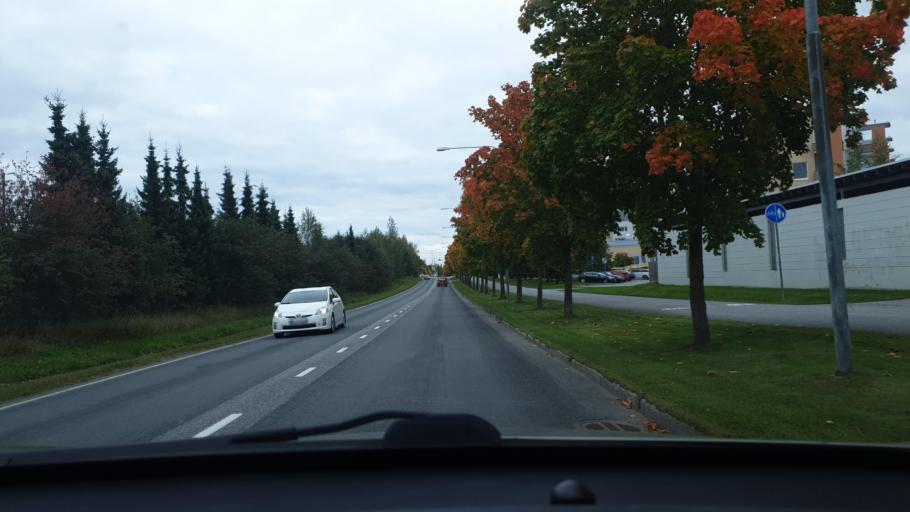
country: FI
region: Ostrobothnia
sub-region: Vaasa
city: Vaasa
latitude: 63.0950
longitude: 21.6289
